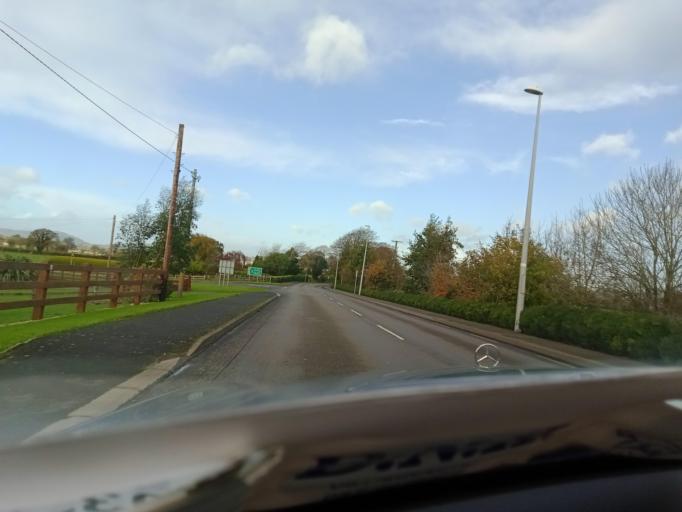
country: IE
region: Leinster
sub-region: Kilkenny
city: Piltown
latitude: 52.3371
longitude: -7.3191
